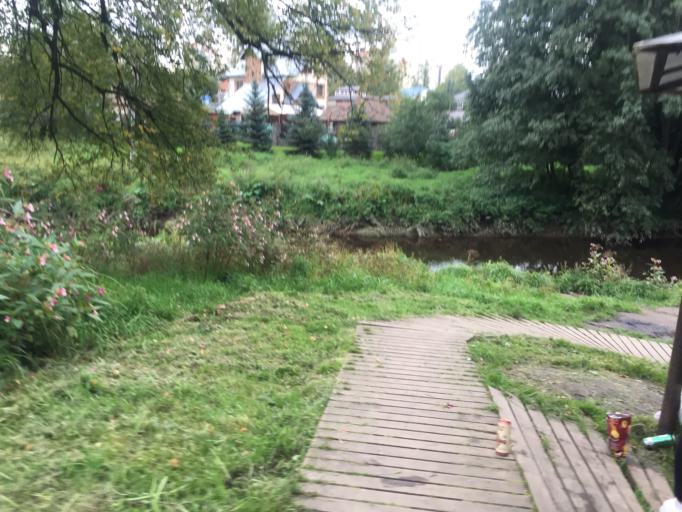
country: RU
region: Leningrad
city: Murino
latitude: 60.0492
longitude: 30.4550
